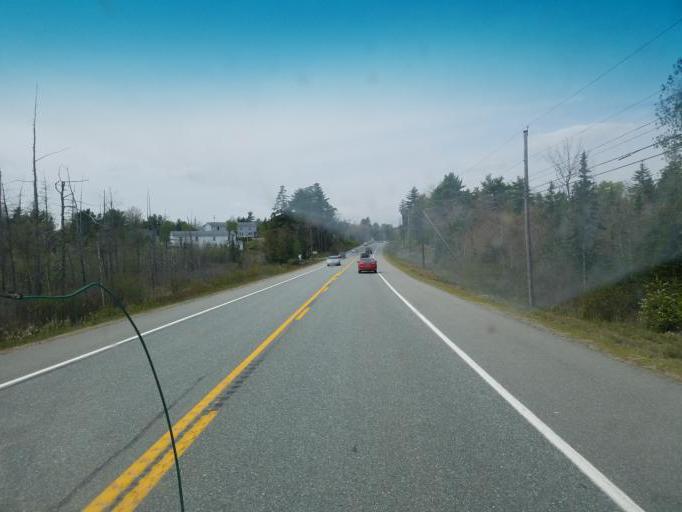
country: US
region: Maine
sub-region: Hancock County
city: Ellsworth
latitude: 44.5827
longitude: -68.4857
